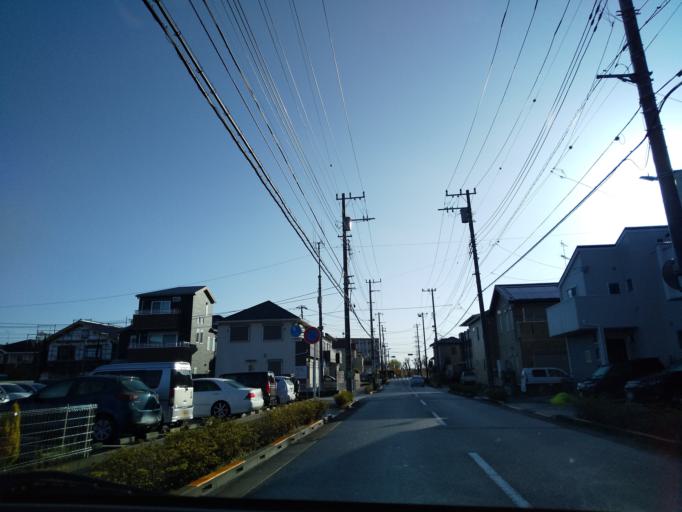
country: JP
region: Tokyo
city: Hino
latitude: 35.6472
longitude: 139.3759
